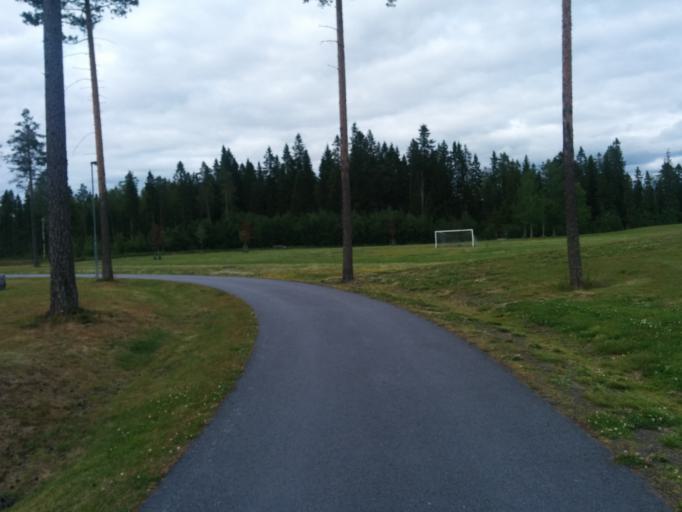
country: SE
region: Vaesterbotten
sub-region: Umea Kommun
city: Ersmark
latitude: 63.8040
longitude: 20.3742
